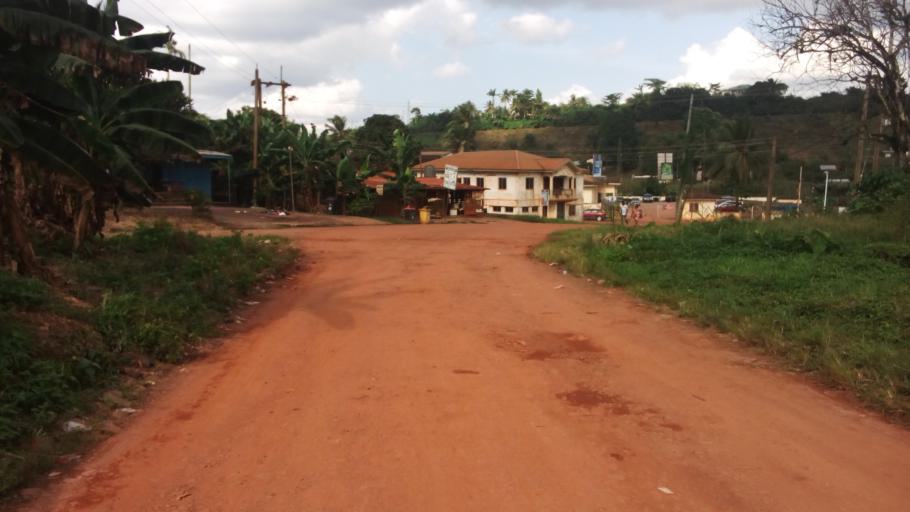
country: GH
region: Western
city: Tarkwa
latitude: 5.3004
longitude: -2.0001
